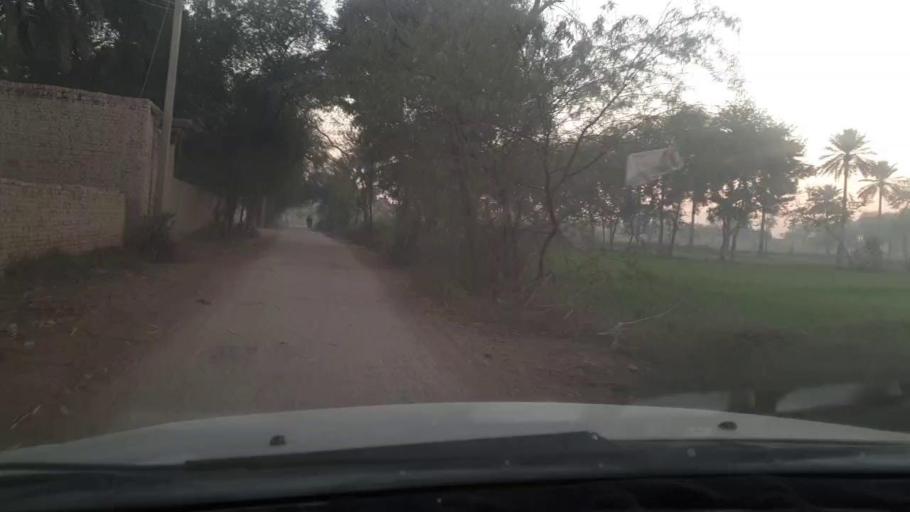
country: PK
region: Sindh
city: Ghotki
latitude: 28.0061
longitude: 69.3378
